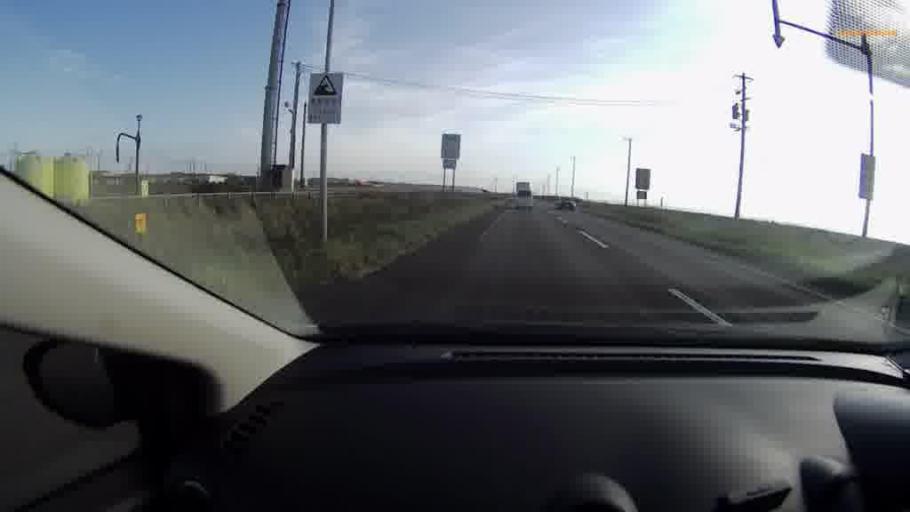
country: JP
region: Hokkaido
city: Kushiro
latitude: 42.9991
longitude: 144.2266
